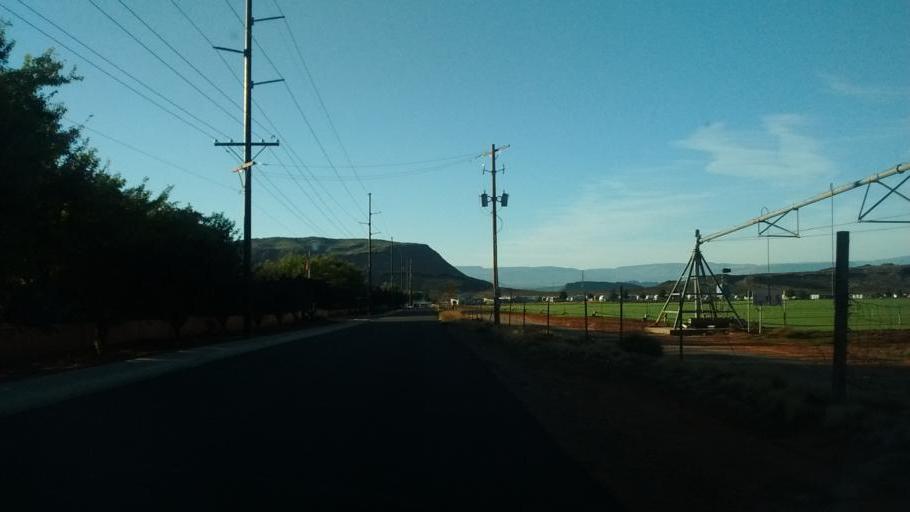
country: US
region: Utah
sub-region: Washington County
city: Washington
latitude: 37.1349
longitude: -113.4910
